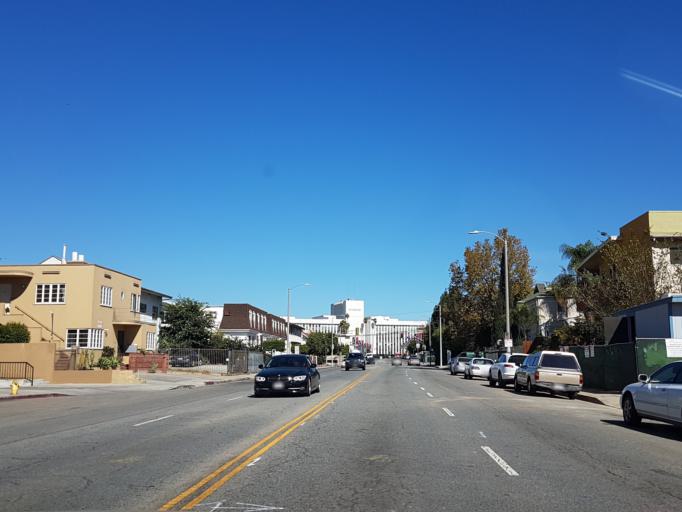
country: US
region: California
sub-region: Los Angeles County
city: Hollywood
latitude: 34.0578
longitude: -118.3212
